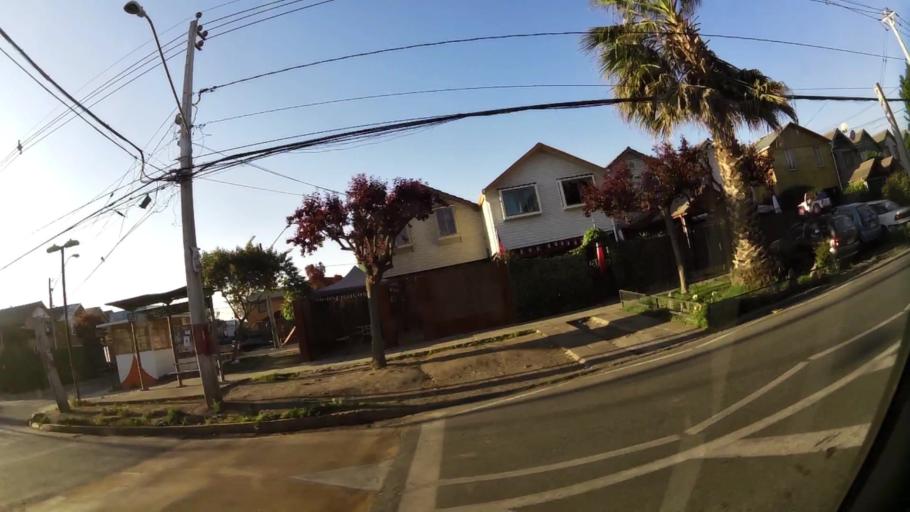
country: CL
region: Santiago Metropolitan
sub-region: Provincia de Santiago
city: Lo Prado
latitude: -33.4743
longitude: -70.7544
